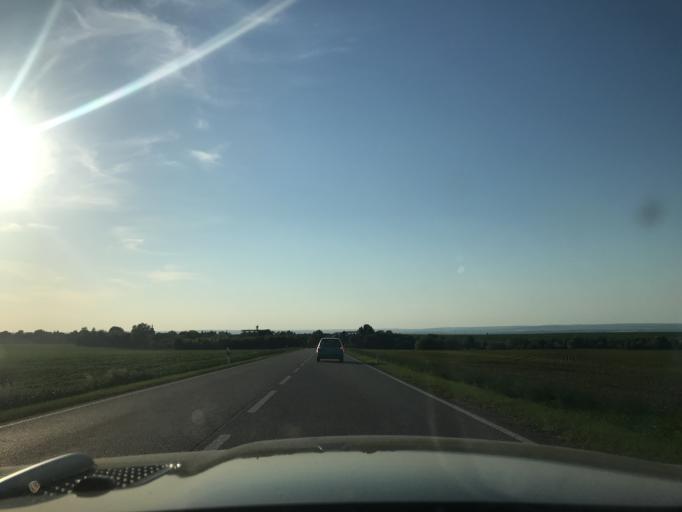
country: DE
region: Thuringia
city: Bad Langensalza
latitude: 51.0647
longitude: 10.6440
